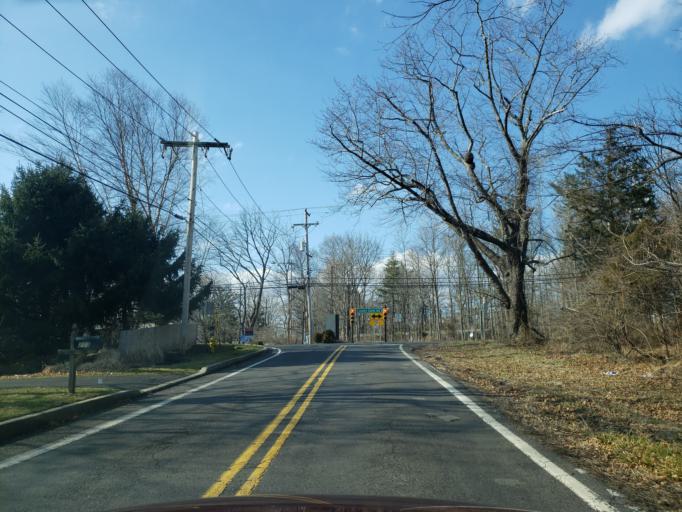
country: US
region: Pennsylvania
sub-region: Bucks County
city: Doylestown
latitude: 40.2951
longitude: -75.1473
